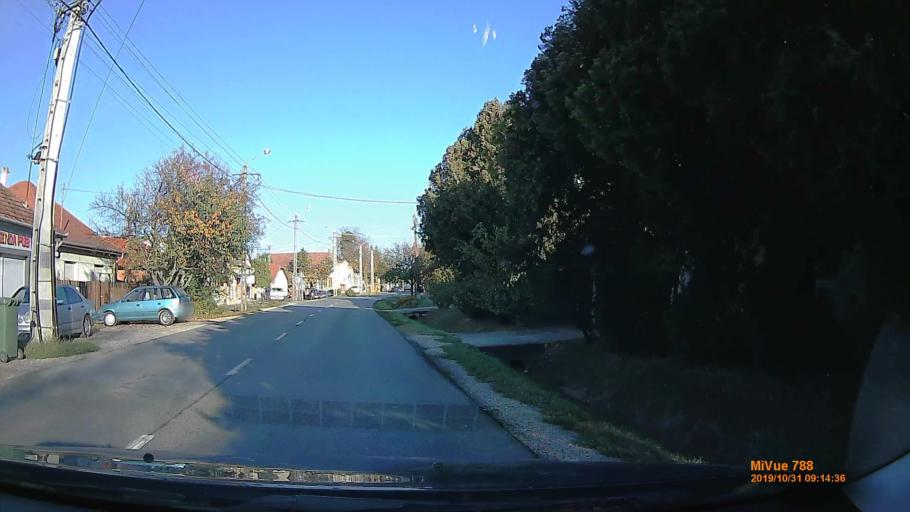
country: HU
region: Pest
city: Peteri
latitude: 47.3876
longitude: 19.4104
